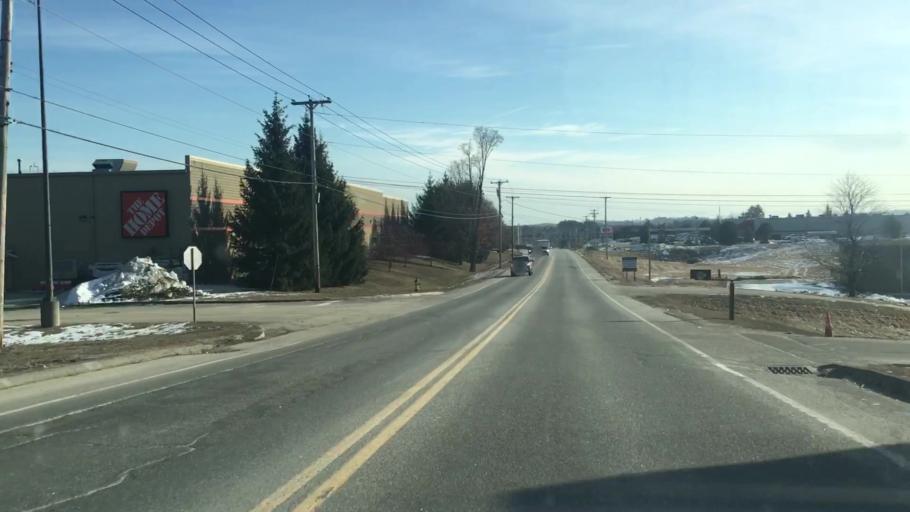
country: US
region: Maine
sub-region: Androscoggin County
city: Auburn
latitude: 44.1224
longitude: -70.2415
